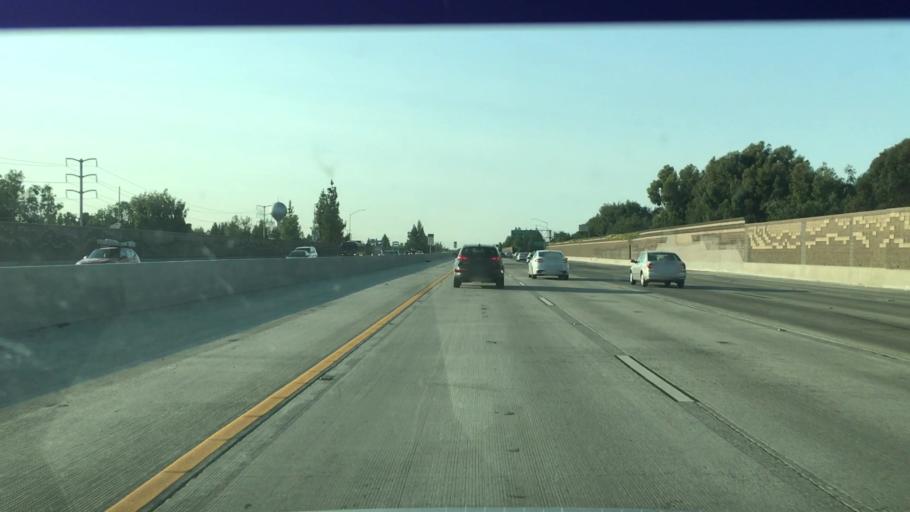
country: US
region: California
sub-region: San Joaquin County
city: Lincoln Village
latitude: 37.9993
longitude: -121.3492
